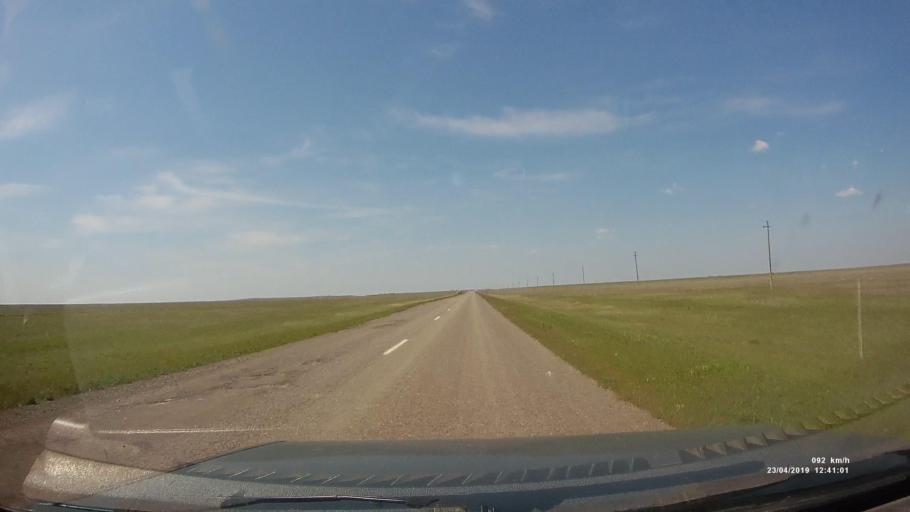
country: RU
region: Kalmykiya
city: Yashalta
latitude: 46.4449
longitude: 42.6875
